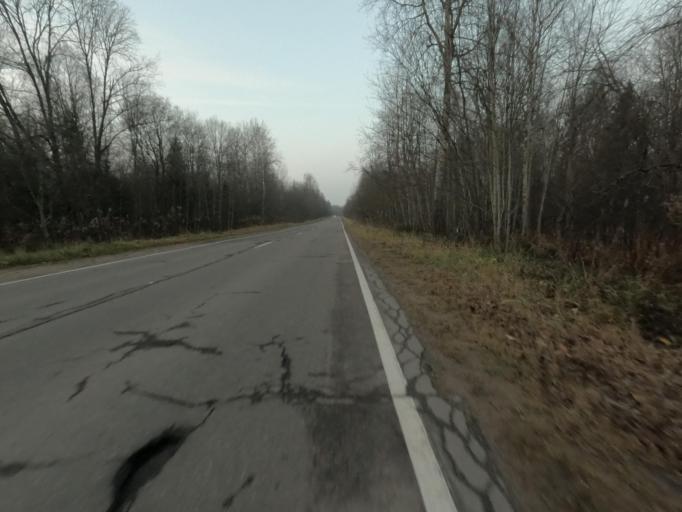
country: RU
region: Leningrad
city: Kirovsk
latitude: 59.8537
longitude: 30.9928
